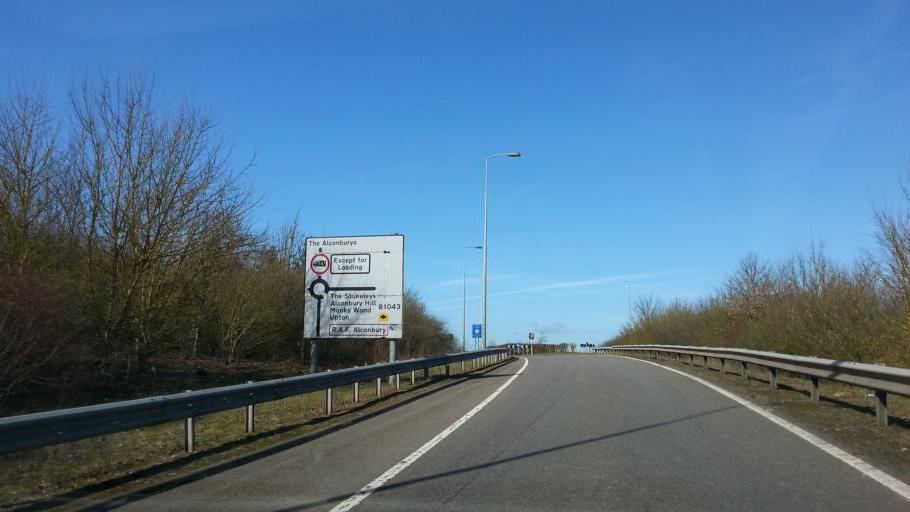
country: GB
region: England
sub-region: Cambridgeshire
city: Great Stukeley
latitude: 52.3611
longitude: -0.2557
